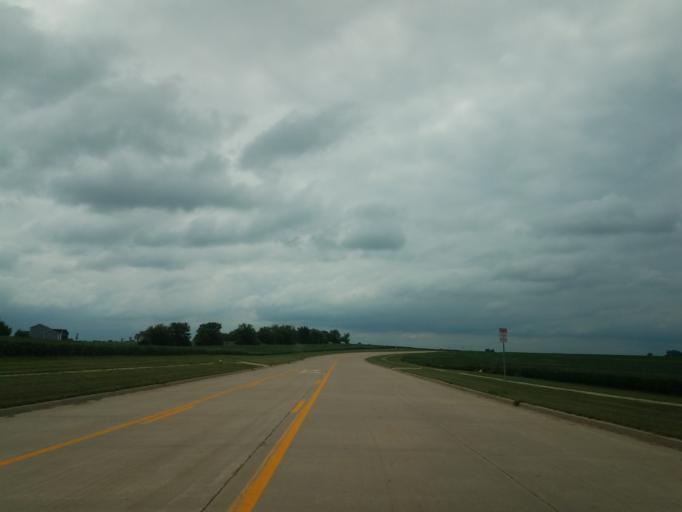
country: US
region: Illinois
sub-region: McLean County
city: Twin Grove
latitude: 40.4428
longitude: -89.0501
